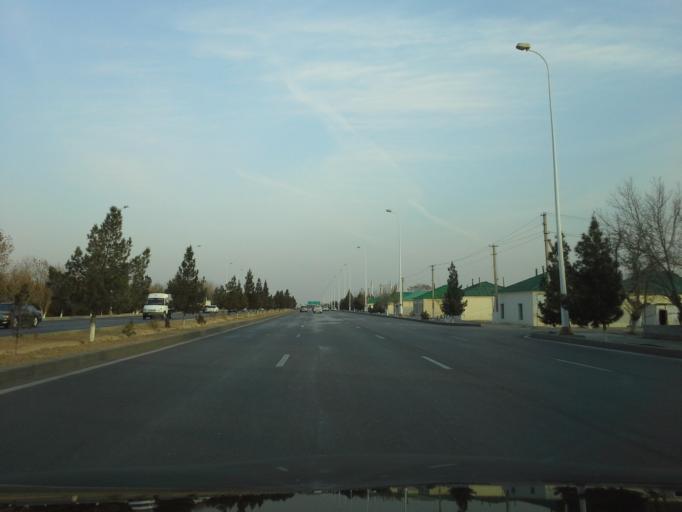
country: TM
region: Ahal
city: Abadan
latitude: 38.0289
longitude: 58.2336
